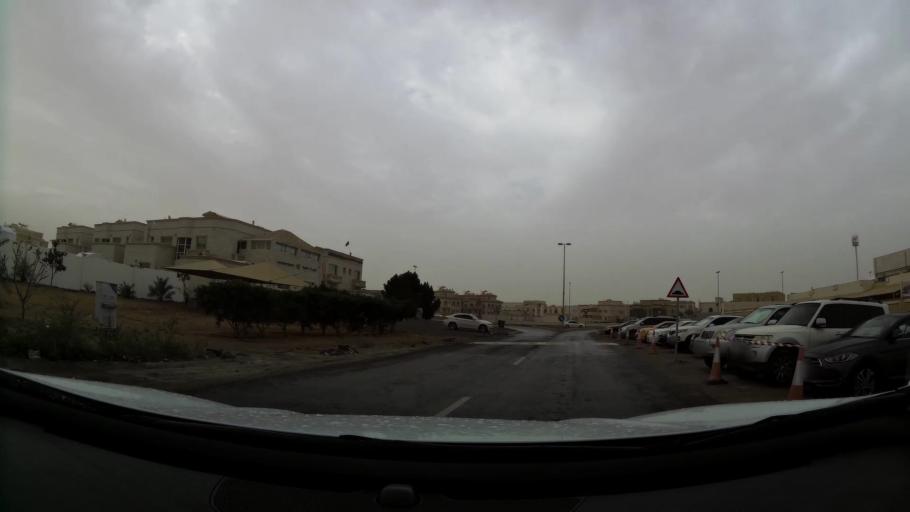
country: AE
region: Abu Dhabi
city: Abu Dhabi
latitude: 24.4285
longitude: 54.5853
